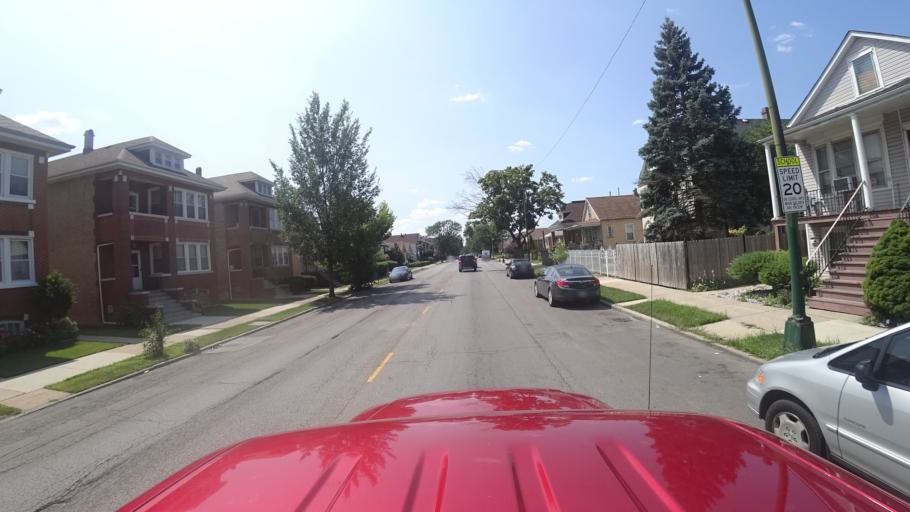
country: US
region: Illinois
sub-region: Cook County
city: Chicago
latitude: 41.7981
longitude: -87.6940
